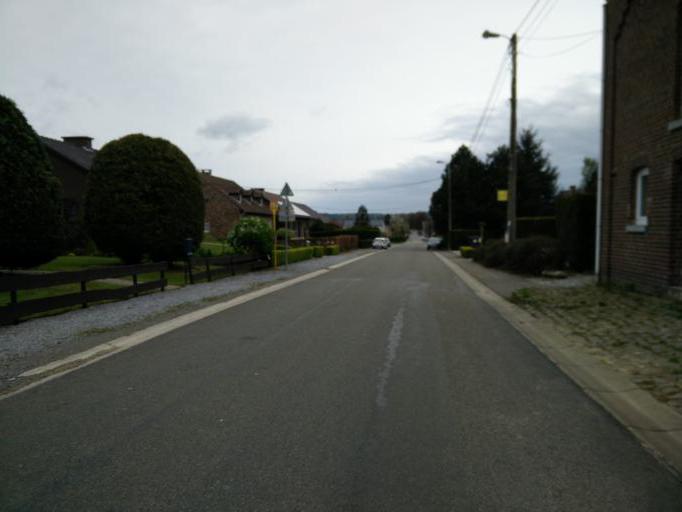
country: BE
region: Wallonia
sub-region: Province de Liege
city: Dalhem
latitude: 50.7334
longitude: 5.7562
